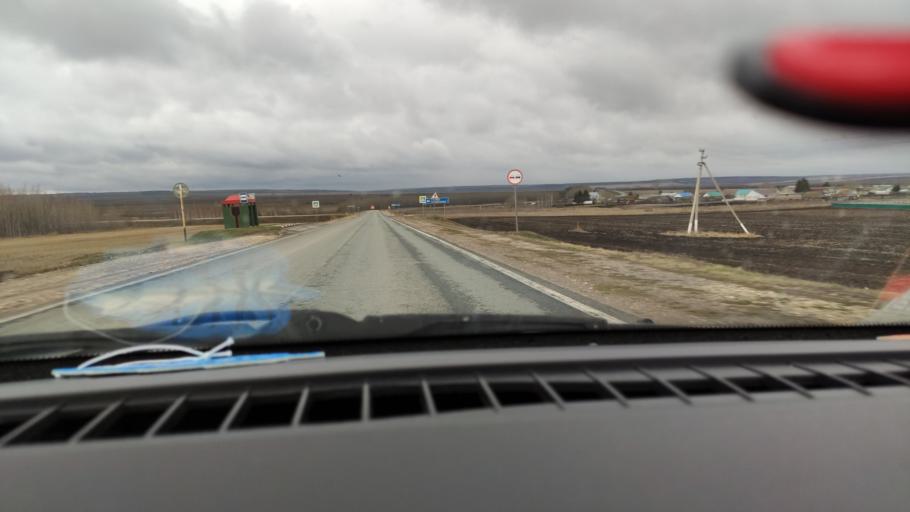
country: RU
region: Tatarstan
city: Cheremshan
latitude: 54.8018
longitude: 51.4986
